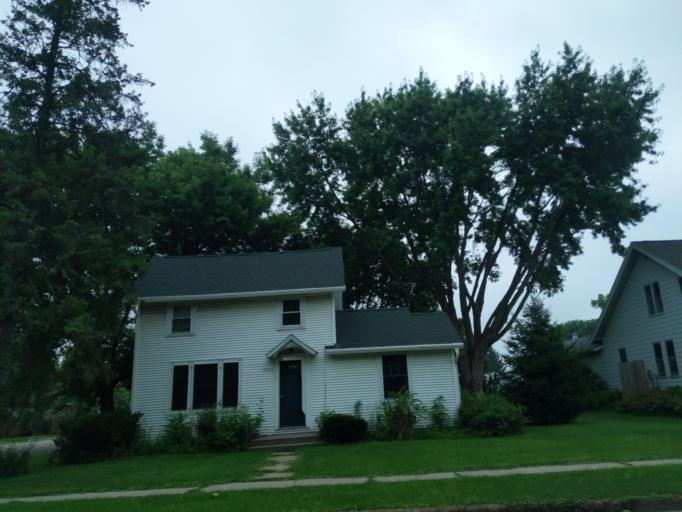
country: US
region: Wisconsin
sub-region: Dane County
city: Black Earth
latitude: 43.1352
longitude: -89.7480
